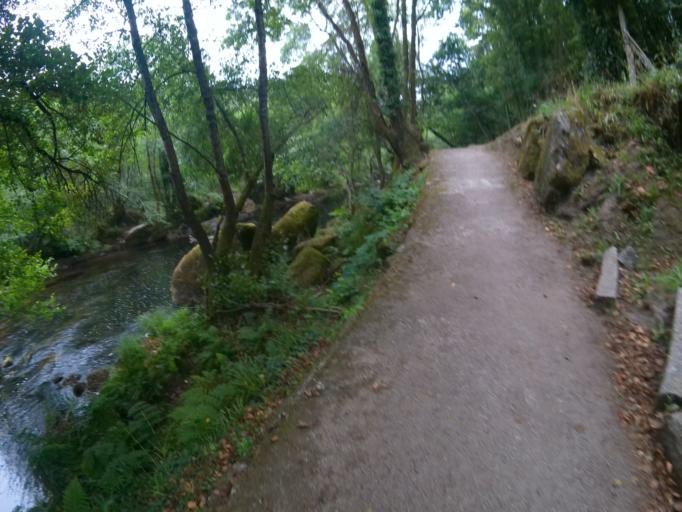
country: PT
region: Viana do Castelo
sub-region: Ponte da Barca
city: Ponte da Barca
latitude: 41.8110
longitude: -8.4300
